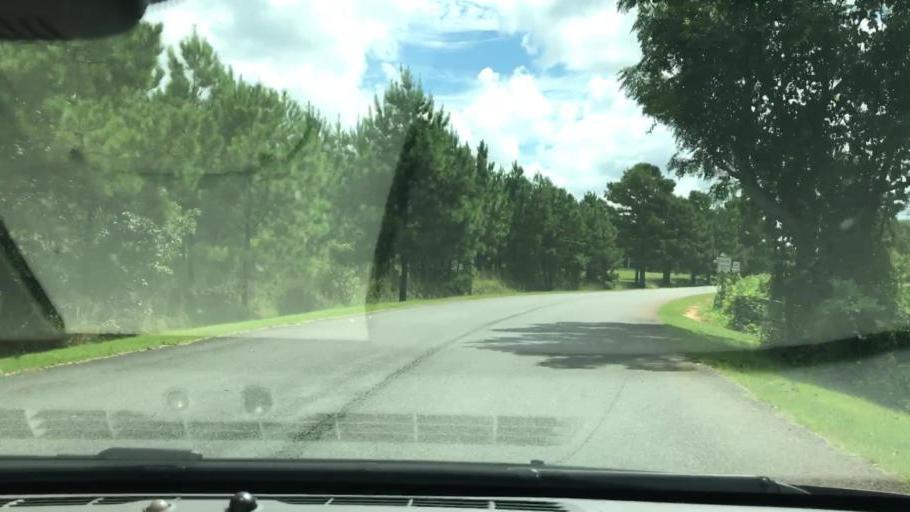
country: US
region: Georgia
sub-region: Stewart County
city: Lumpkin
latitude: 32.0707
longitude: -84.9092
